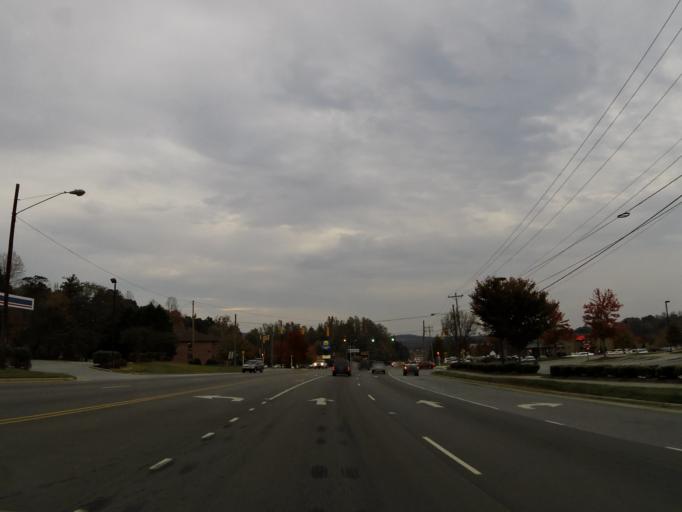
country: US
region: North Carolina
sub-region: Caldwell County
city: Lenoir
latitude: 35.9308
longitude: -81.5275
